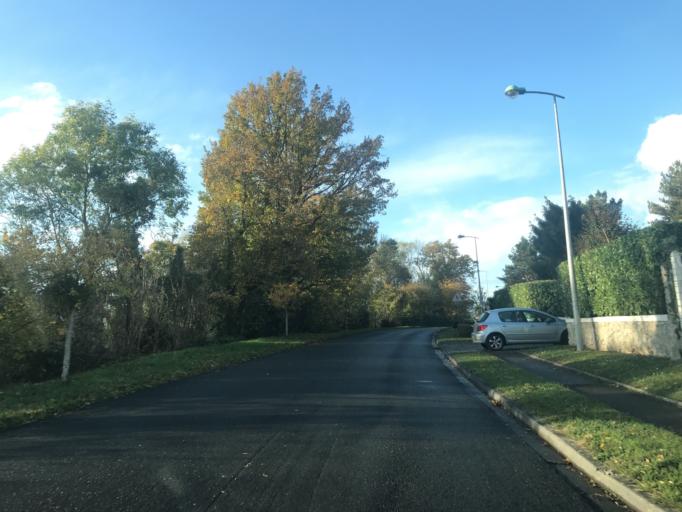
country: FR
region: Haute-Normandie
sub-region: Departement de l'Eure
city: Saint-Aubin-sur-Gaillon
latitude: 49.0844
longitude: 1.2929
